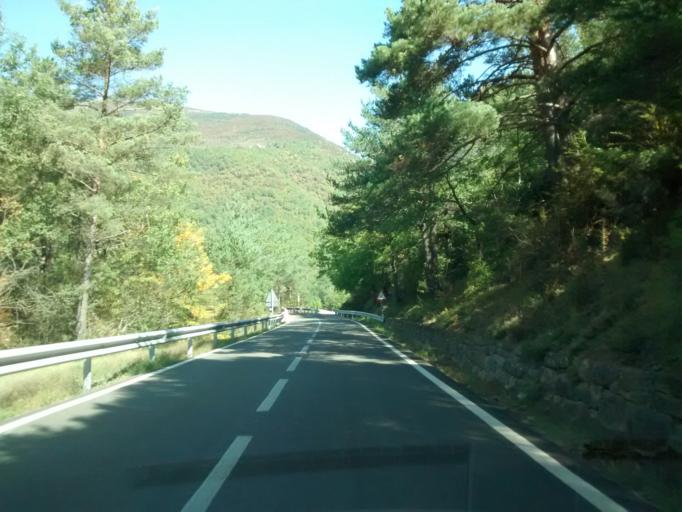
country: ES
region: Aragon
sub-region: Provincia de Huesca
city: Fiscal
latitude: 42.5345
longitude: -0.1402
